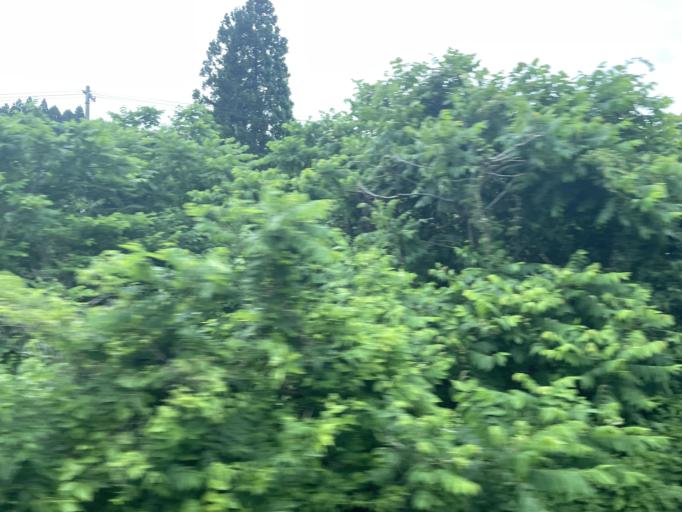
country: JP
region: Akita
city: Tenno
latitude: 39.9039
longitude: 139.8612
